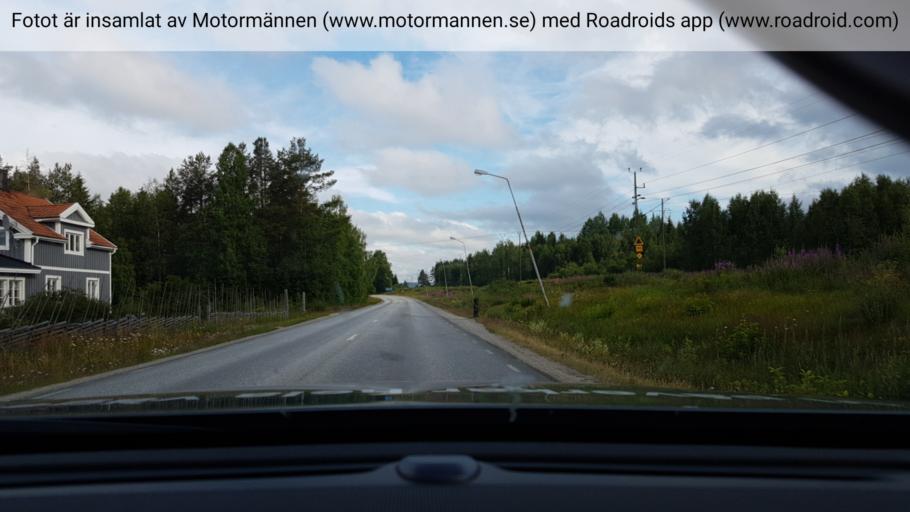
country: SE
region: Vaesterbotten
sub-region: Vindelns Kommun
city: Vindeln
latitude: 64.2132
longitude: 19.7138
